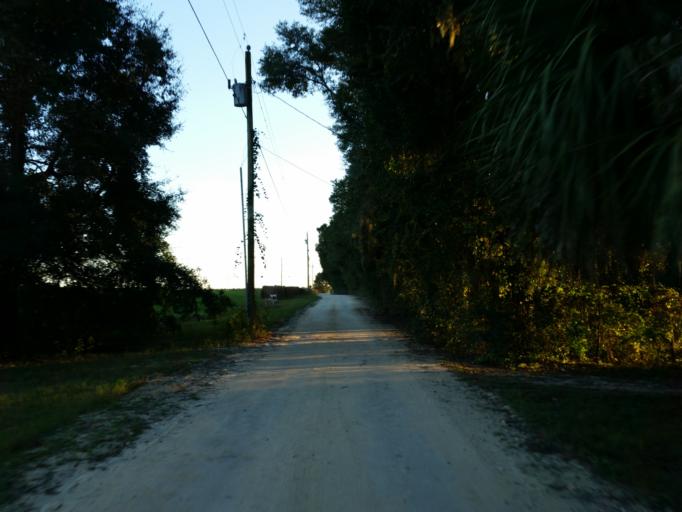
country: US
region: Florida
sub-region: Hernando County
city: Hill 'n Dale
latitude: 28.5258
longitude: -82.2508
